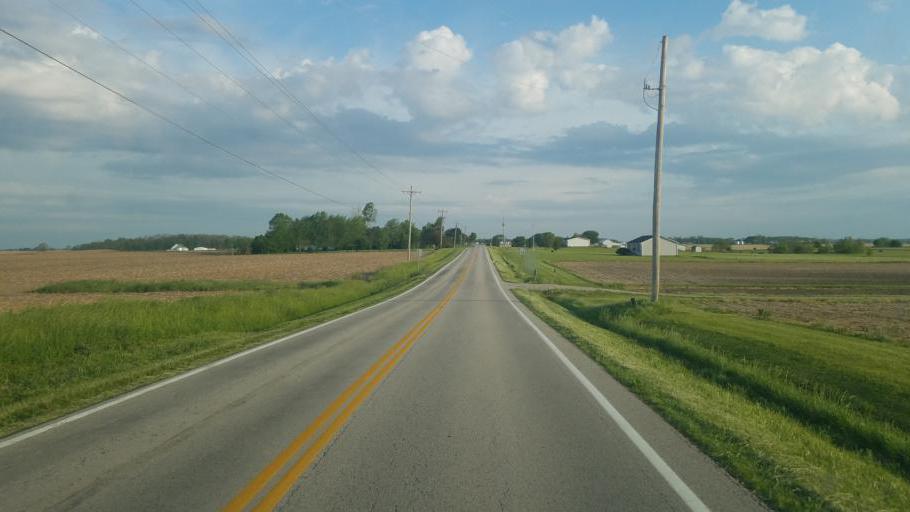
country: US
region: Ohio
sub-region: Clinton County
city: Sabina
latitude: 39.4369
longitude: -83.6346
